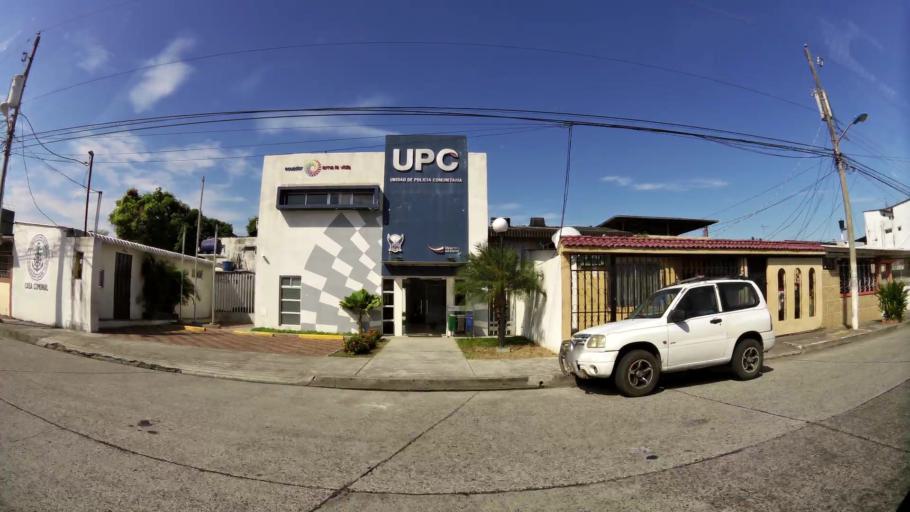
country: EC
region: Guayas
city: Guayaquil
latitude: -2.2276
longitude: -79.8946
